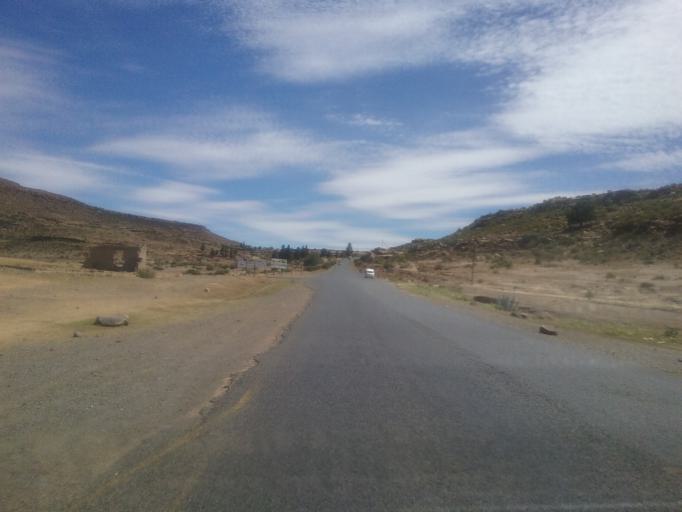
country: LS
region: Mohale's Hoek District
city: Mohale's Hoek
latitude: -30.0849
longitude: 27.4293
